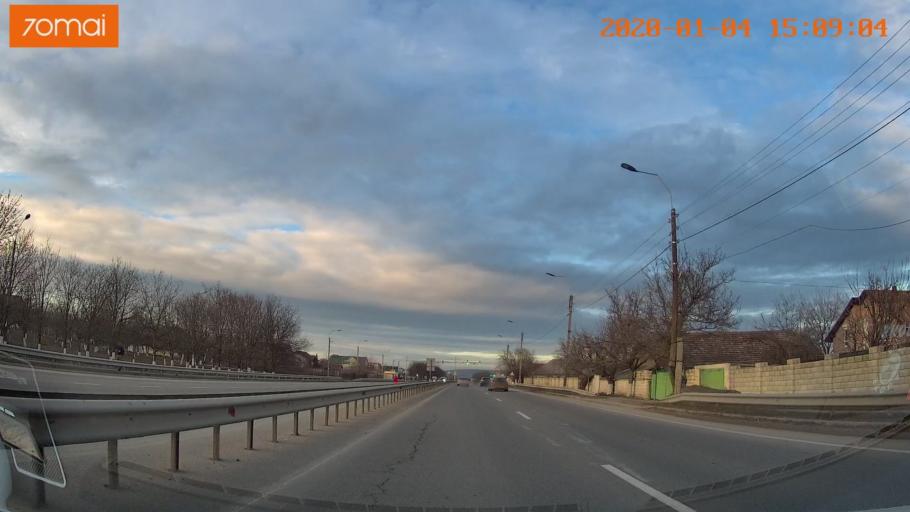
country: MD
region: Chisinau
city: Cricova
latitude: 47.1463
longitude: 28.8324
